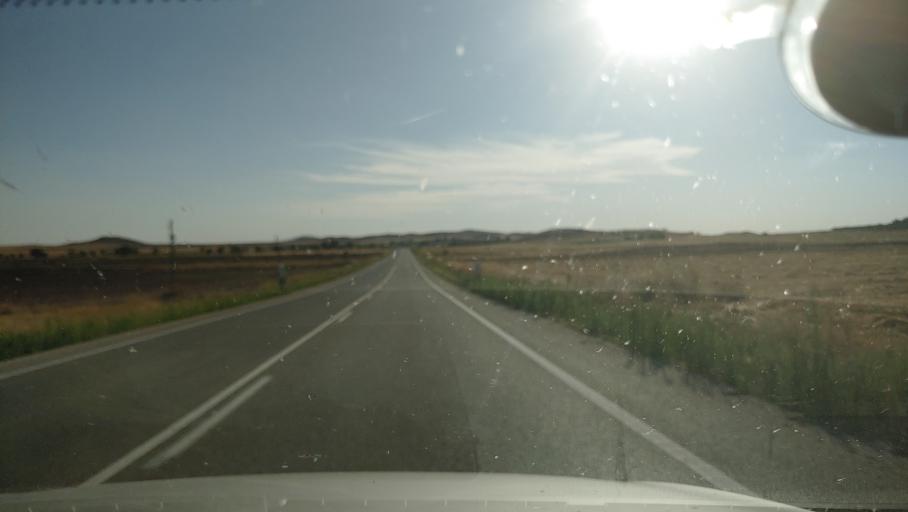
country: ES
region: Castille-La Mancha
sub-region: Provincia de Ciudad Real
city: Fuenllana
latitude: 38.7617
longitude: -2.9395
